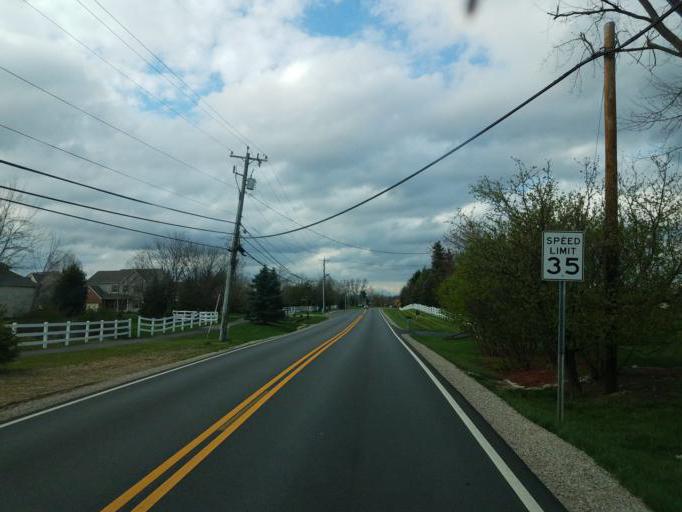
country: US
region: Ohio
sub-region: Delaware County
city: Powell
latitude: 40.1752
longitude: -83.0779
